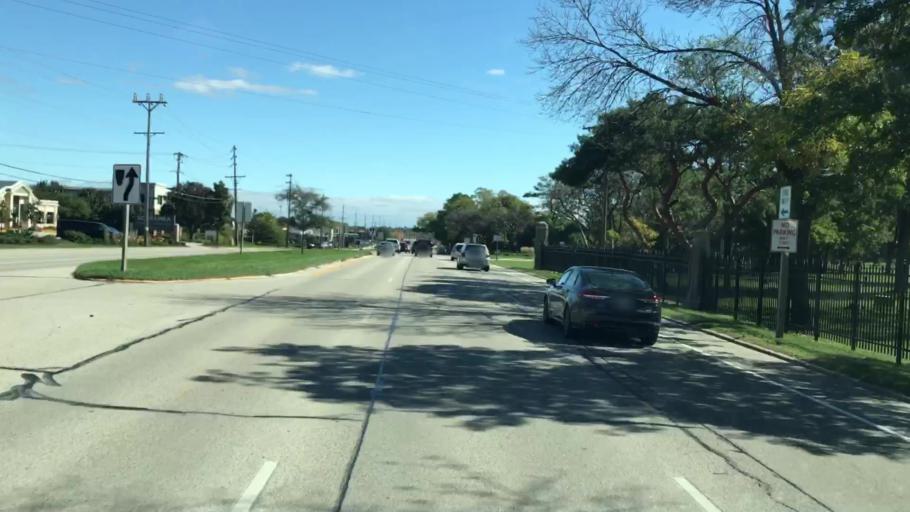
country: US
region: Wisconsin
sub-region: Waukesha County
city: Butler
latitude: 43.0893
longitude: -88.0778
